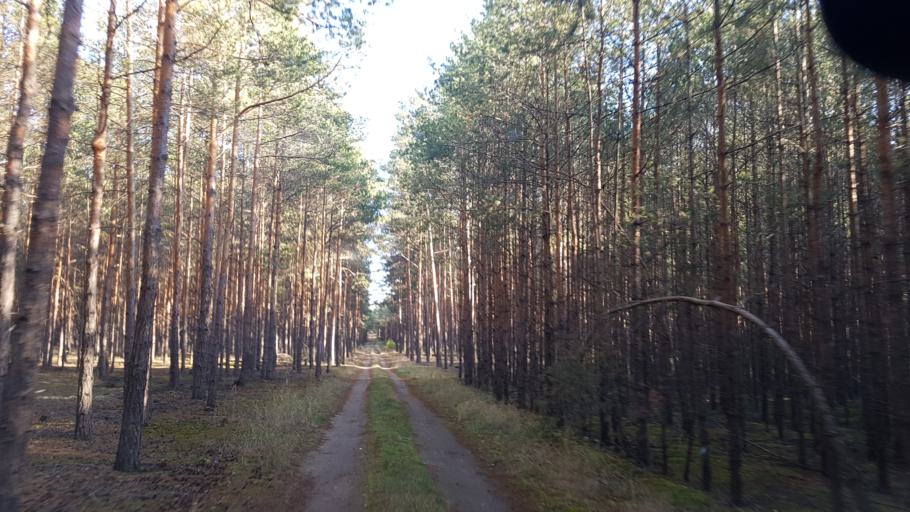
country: DE
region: Brandenburg
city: Sonnewalde
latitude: 51.6465
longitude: 13.6408
